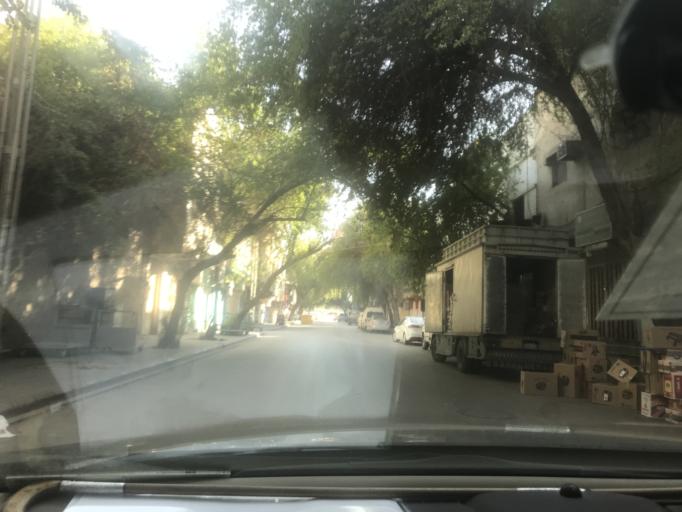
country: SA
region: Ar Riyad
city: Riyadh
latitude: 24.6261
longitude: 46.7079
